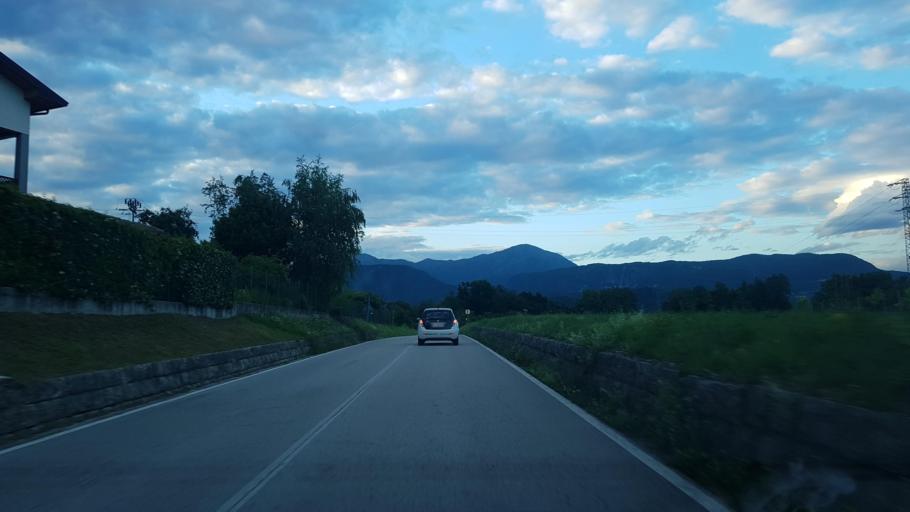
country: IT
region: Friuli Venezia Giulia
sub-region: Provincia di Pordenone
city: Pinzano al Tagliamento
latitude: 46.1922
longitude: 12.9515
